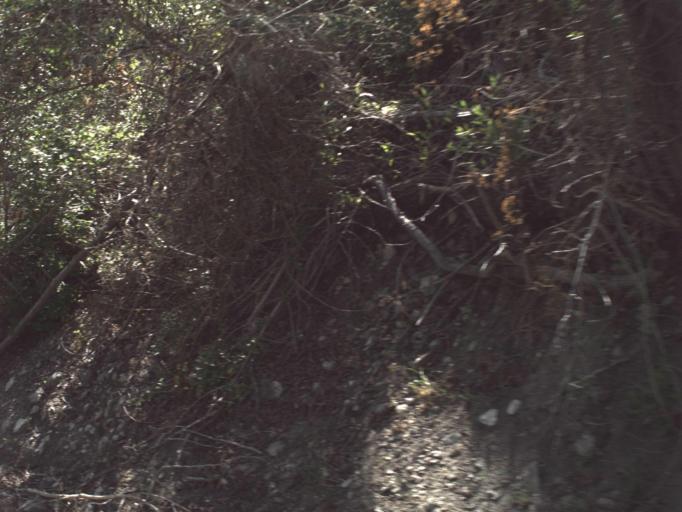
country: US
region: Utah
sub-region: Weber County
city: Liberty
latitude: 41.2542
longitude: -111.8735
